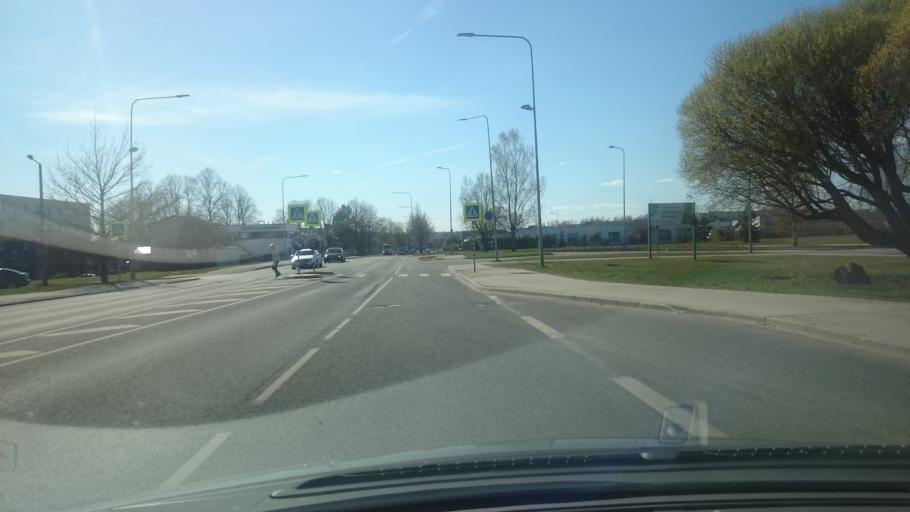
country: EE
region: Tartu
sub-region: Tartu linn
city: Tartu
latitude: 58.3801
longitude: 26.7639
